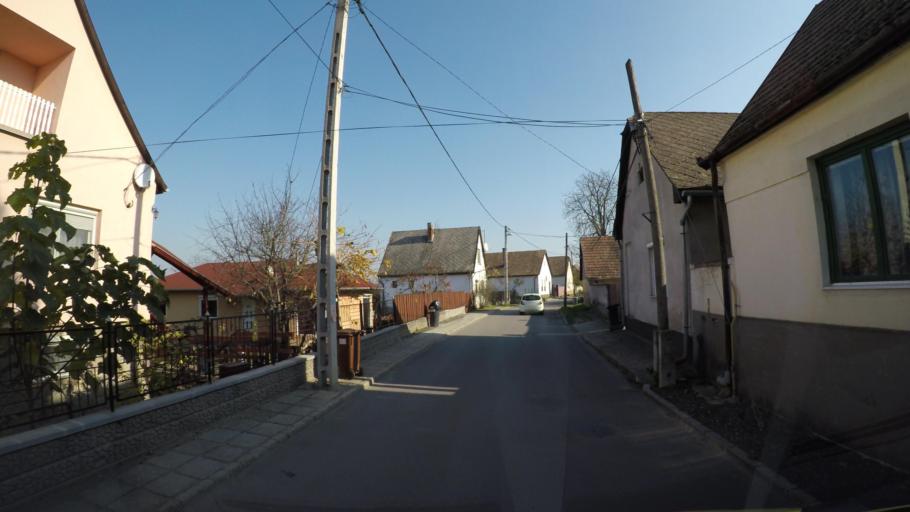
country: HU
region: Pest
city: Leanyfalu
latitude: 47.6912
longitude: 19.1023
